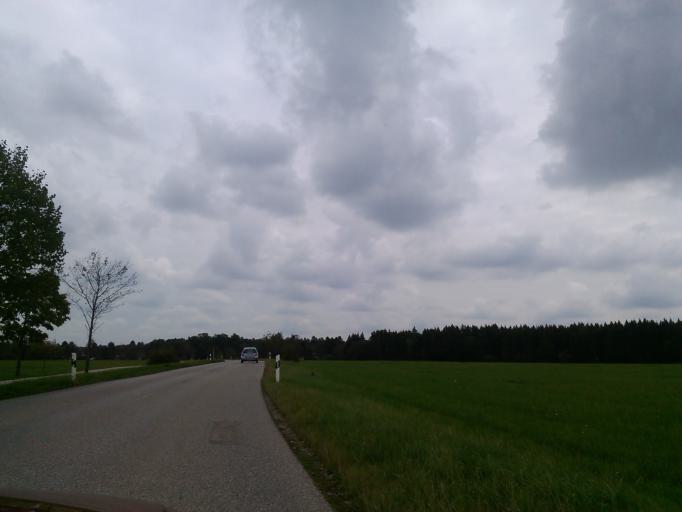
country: DE
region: Bavaria
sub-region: Upper Bavaria
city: Krailling
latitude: 48.1012
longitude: 11.3937
